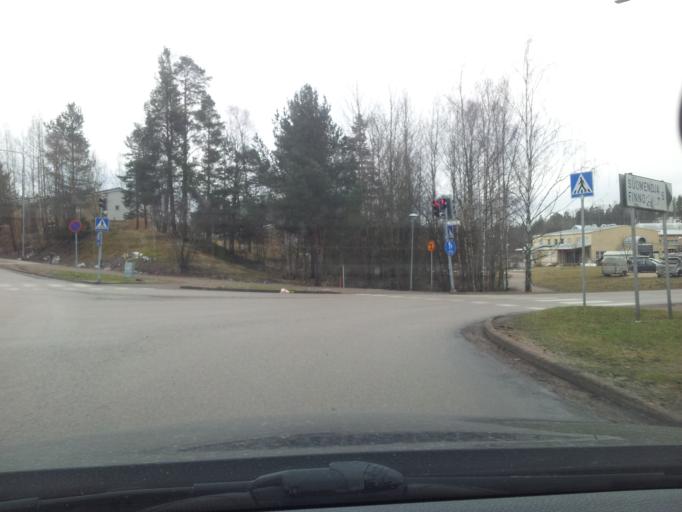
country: FI
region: Uusimaa
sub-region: Helsinki
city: Espoo
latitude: 60.1976
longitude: 24.6701
